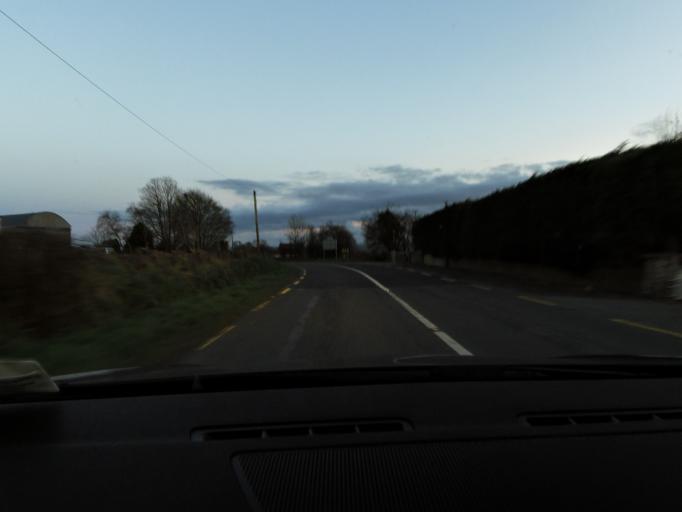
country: IE
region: Connaught
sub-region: Roscommon
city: Boyle
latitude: 53.8429
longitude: -8.2240
